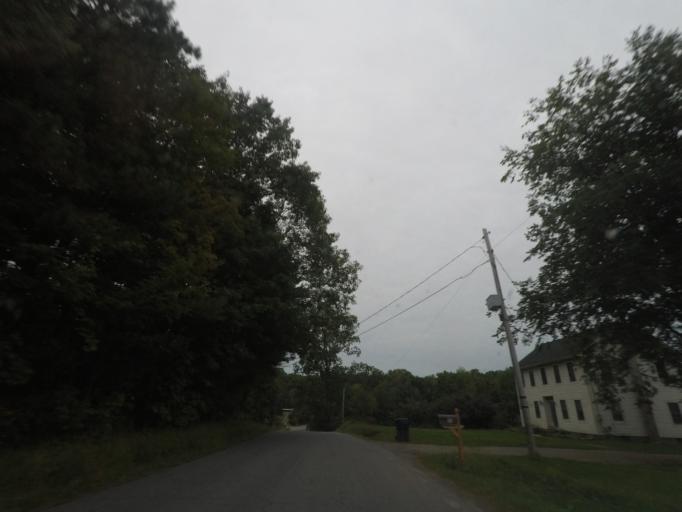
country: US
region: New York
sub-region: Rensselaer County
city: West Sand Lake
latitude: 42.5861
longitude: -73.6036
